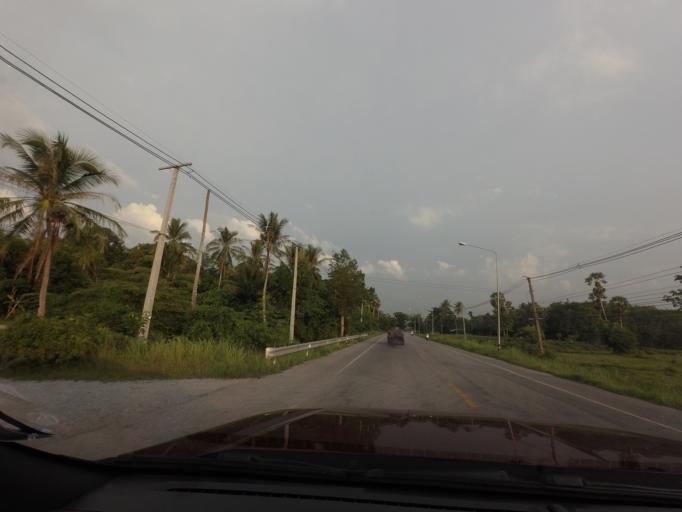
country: TH
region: Pattani
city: Mae Lan
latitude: 6.6375
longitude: 101.1855
